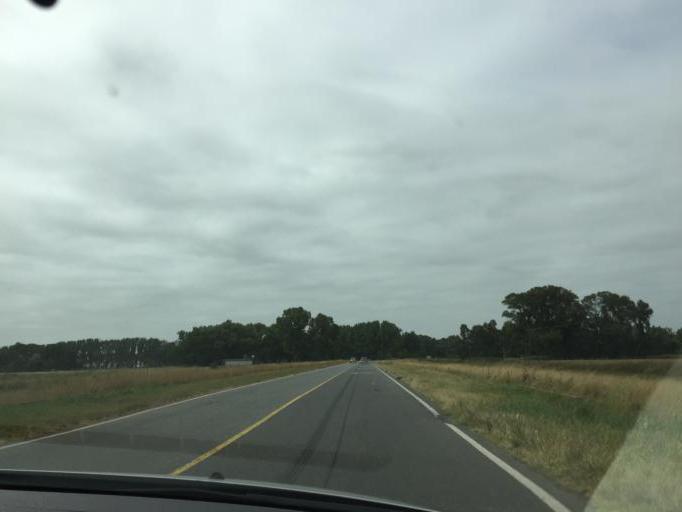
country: AR
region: Buenos Aires
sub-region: Partido de Las Flores
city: Las Flores
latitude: -36.2132
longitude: -59.0459
